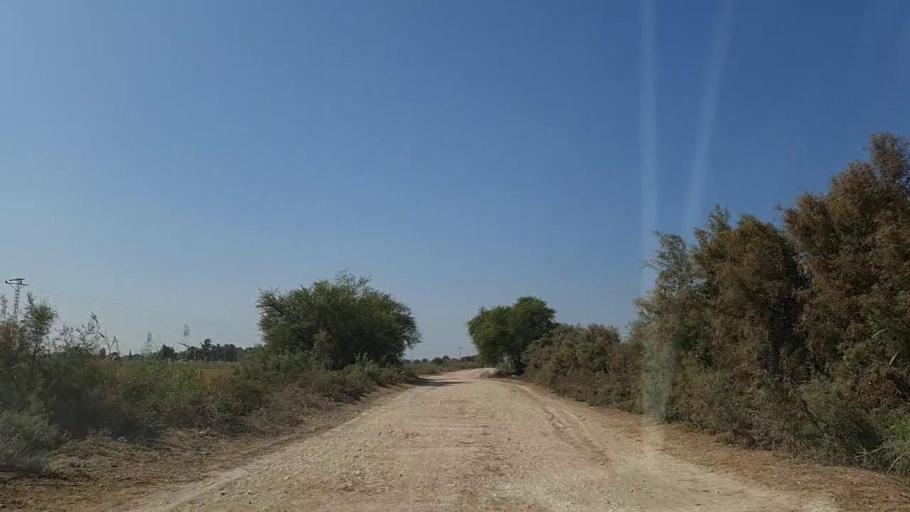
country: PK
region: Sindh
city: Chuhar Jamali
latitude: 24.4188
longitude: 68.0199
